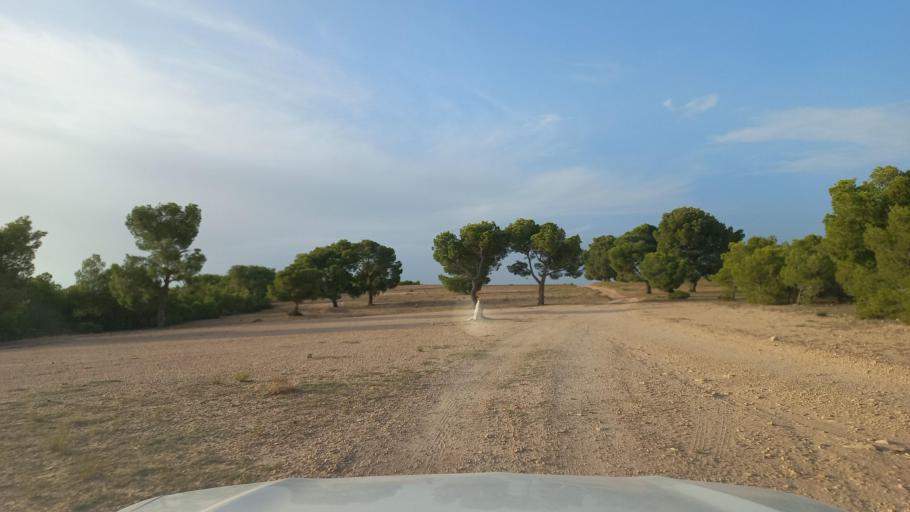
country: TN
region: Al Qasrayn
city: Sbiba
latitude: 35.4126
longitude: 8.8960
